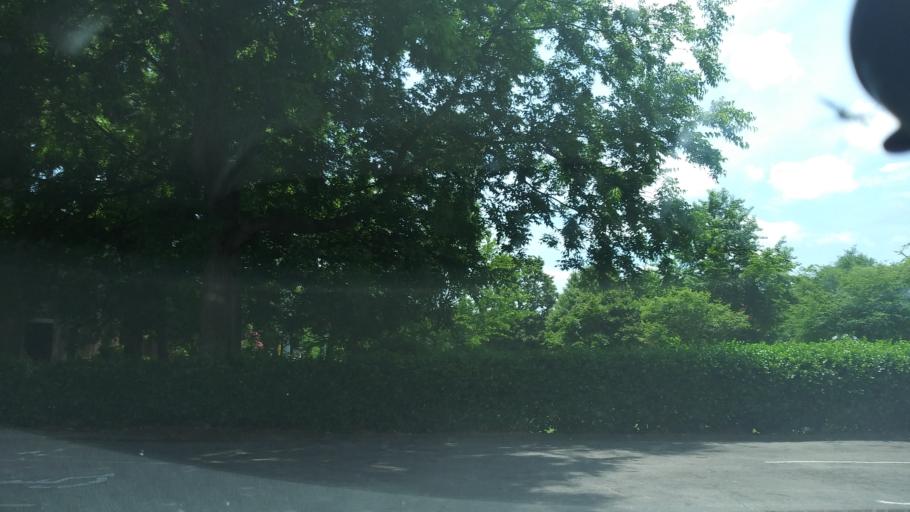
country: US
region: Tennessee
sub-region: Davidson County
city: Belle Meade
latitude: 36.1393
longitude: -86.8417
